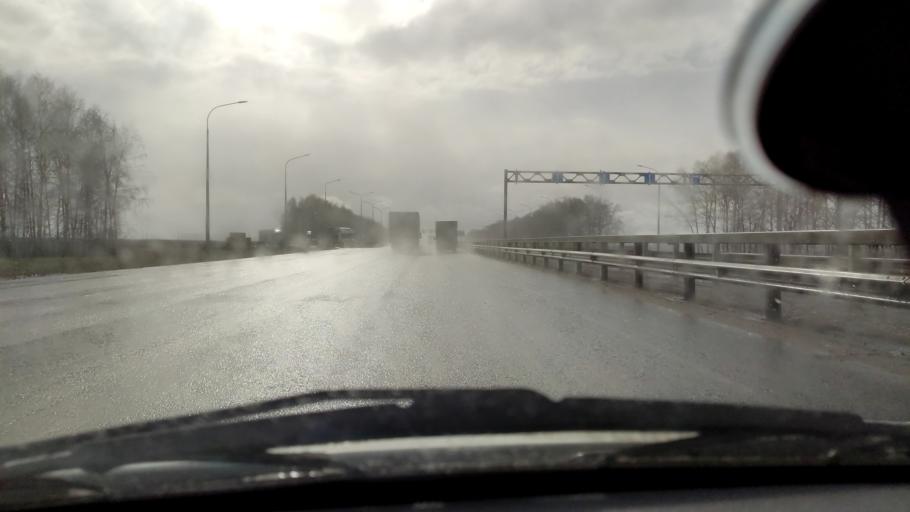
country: RU
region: Bashkortostan
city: Buzdyak
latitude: 54.6452
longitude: 54.5559
